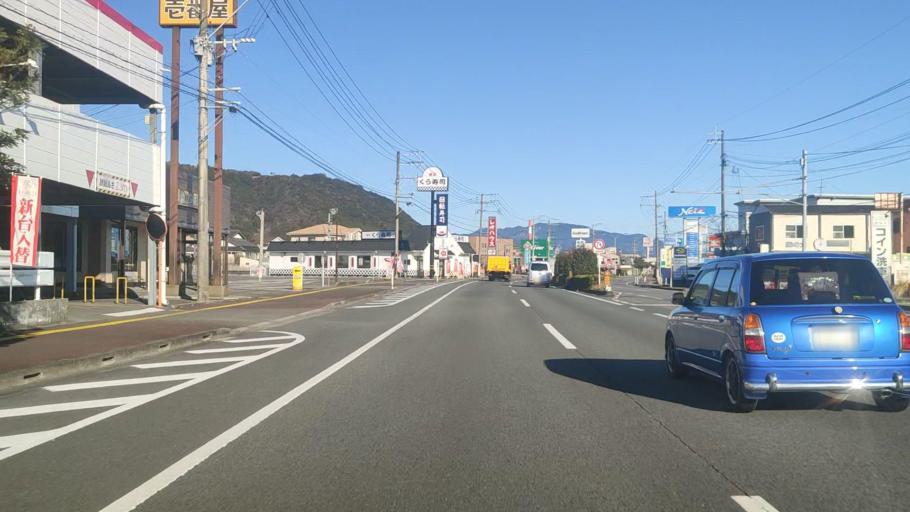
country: JP
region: Miyazaki
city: Nobeoka
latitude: 32.5473
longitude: 131.6773
